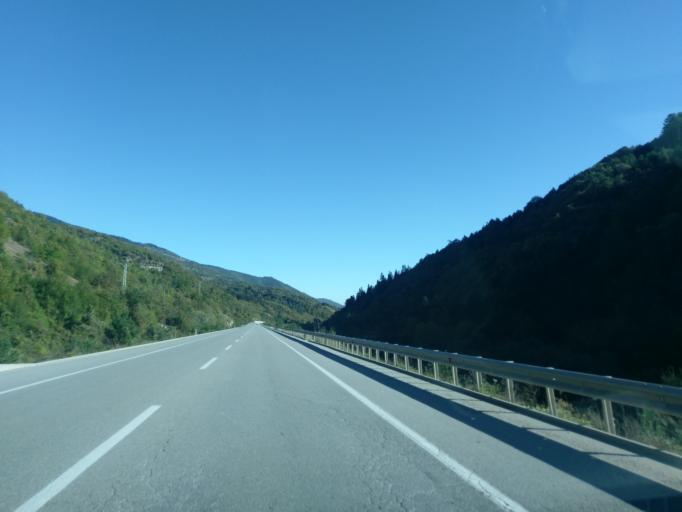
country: TR
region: Sinop
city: Erfelek
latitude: 41.7162
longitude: 34.9351
